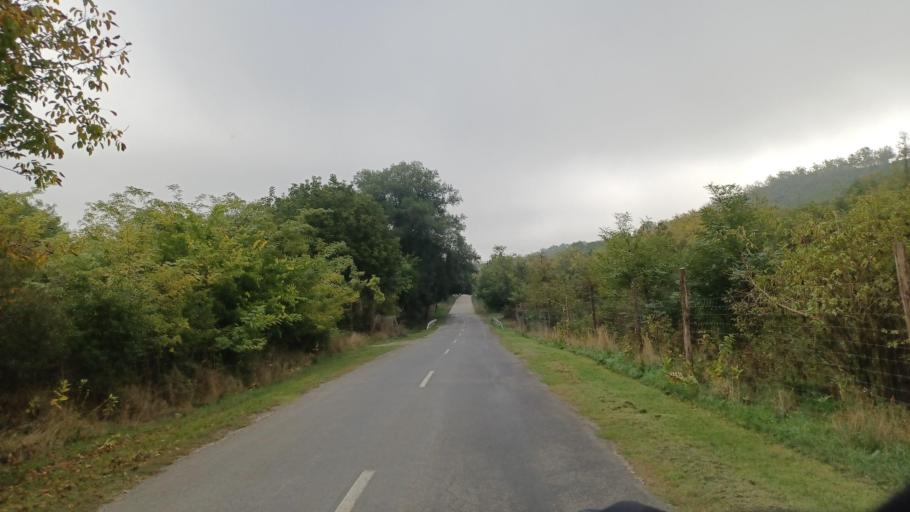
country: HU
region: Tolna
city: Pincehely
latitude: 46.6536
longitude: 18.5084
